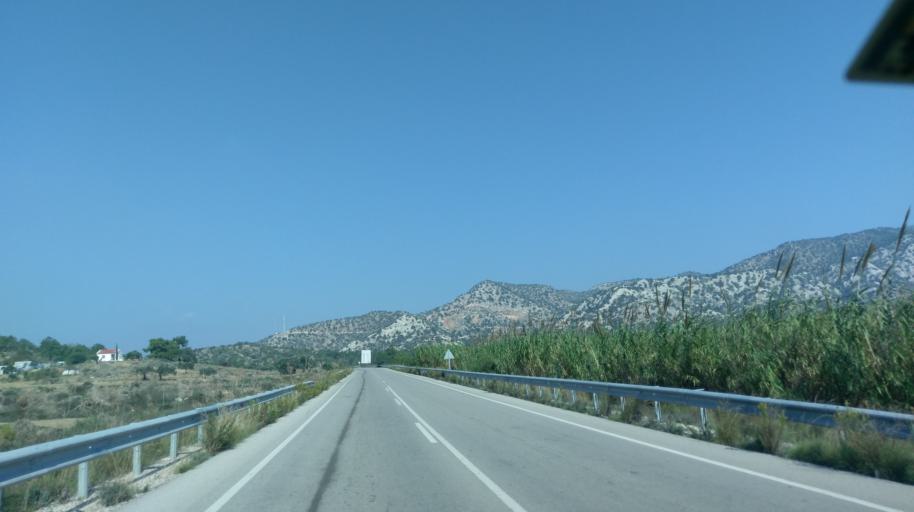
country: CY
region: Ammochostos
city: Lefkonoiko
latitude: 35.3325
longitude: 33.7199
